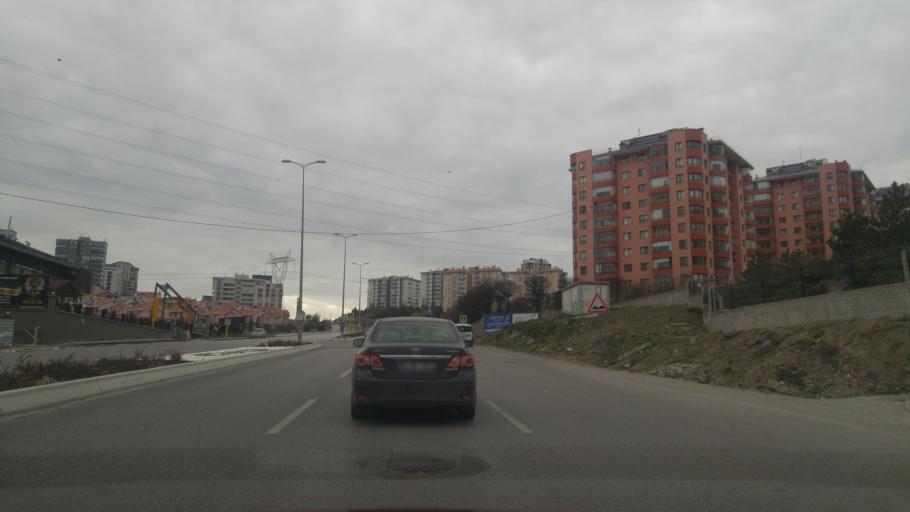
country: TR
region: Ankara
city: Etimesgut
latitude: 39.8602
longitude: 32.6759
